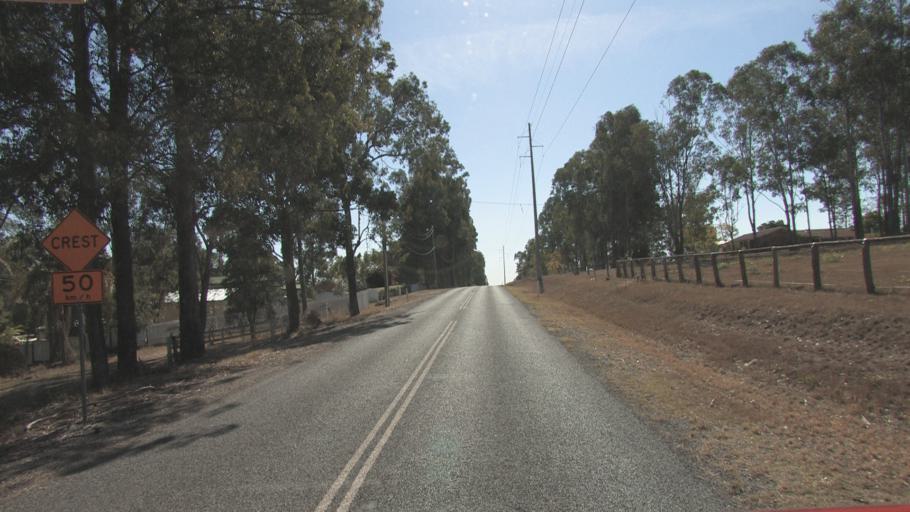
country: AU
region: Queensland
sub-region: Logan
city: Cedar Vale
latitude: -27.8785
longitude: 153.0160
